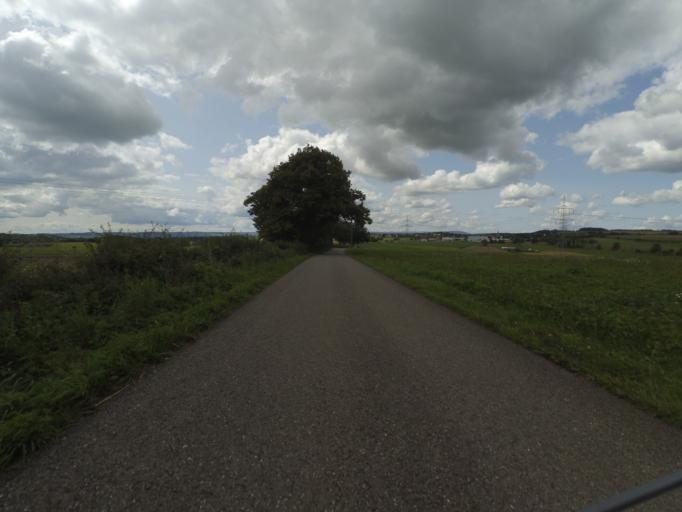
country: DE
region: Baden-Wuerttemberg
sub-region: Freiburg Region
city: Braunlingen
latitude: 47.8907
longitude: 8.4566
